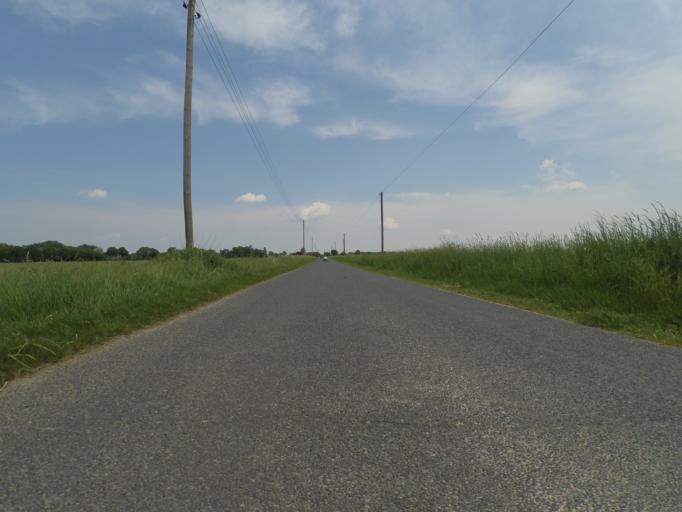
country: DE
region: Lower Saxony
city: Dollbergen
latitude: 52.3483
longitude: 10.1647
